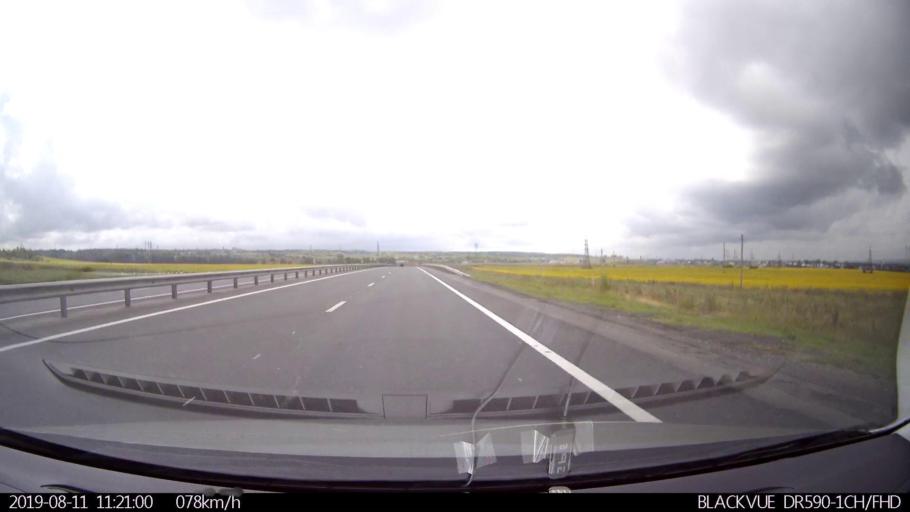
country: RU
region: Ulyanovsk
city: Novoul'yanovsk
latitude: 54.1511
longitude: 48.2642
